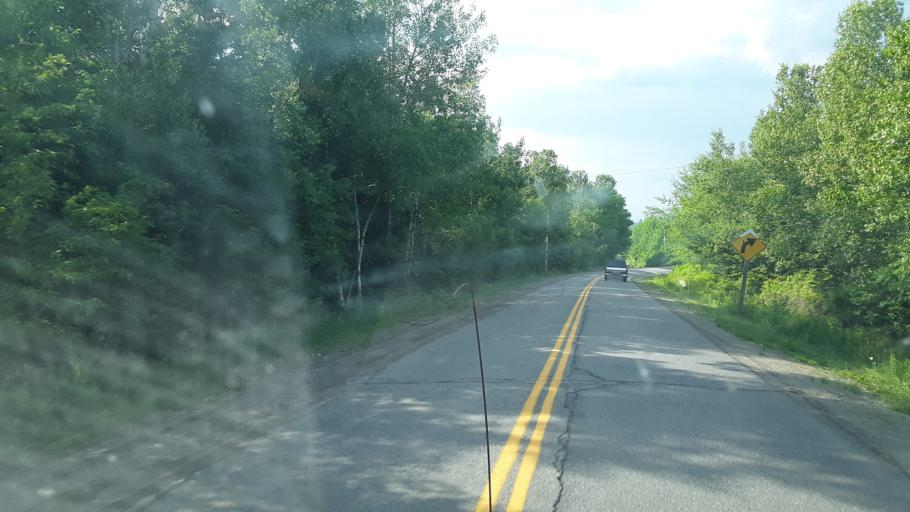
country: US
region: Maine
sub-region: Washington County
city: Calais
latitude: 45.1001
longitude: -67.5106
